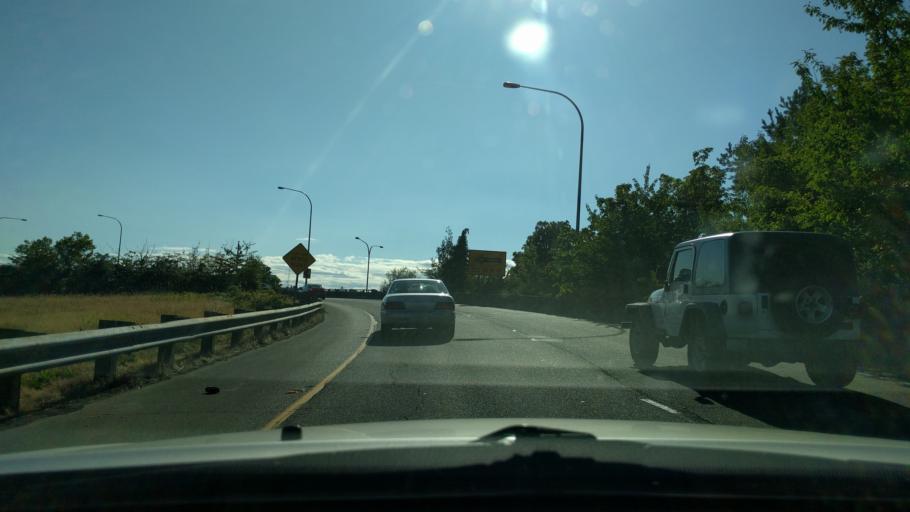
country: US
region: Washington
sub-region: King County
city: Seattle
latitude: 47.6424
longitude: -122.3215
